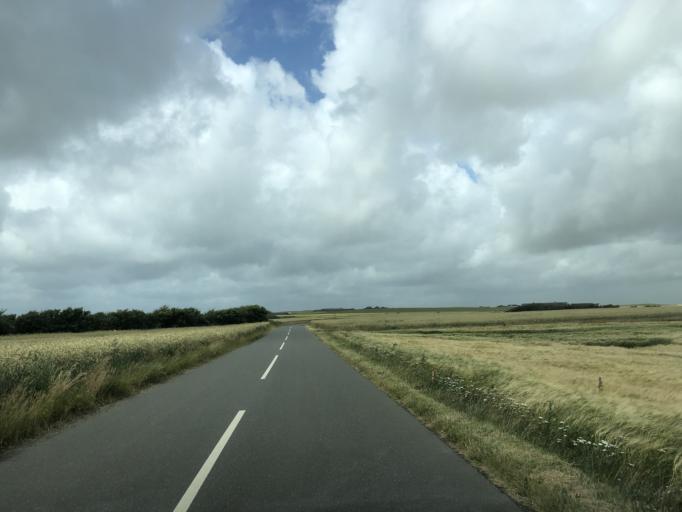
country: DK
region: Central Jutland
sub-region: Lemvig Kommune
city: Harboore
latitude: 56.4946
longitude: 8.1324
